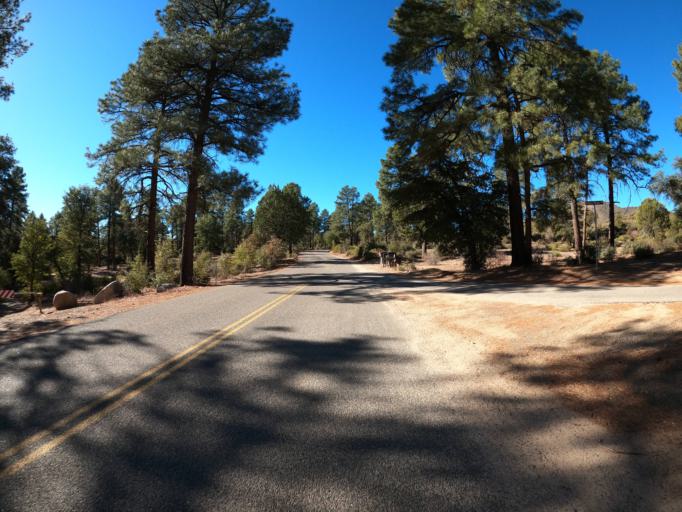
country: US
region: Arizona
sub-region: Yavapai County
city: Verde Village
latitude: 34.5857
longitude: -112.0578
